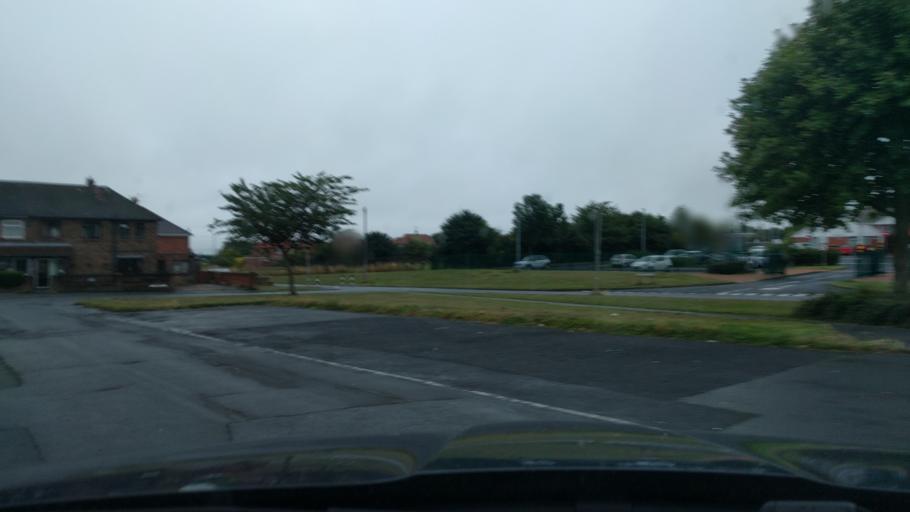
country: GB
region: England
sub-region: Northumberland
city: Bedlington
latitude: 55.1349
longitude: -1.5741
